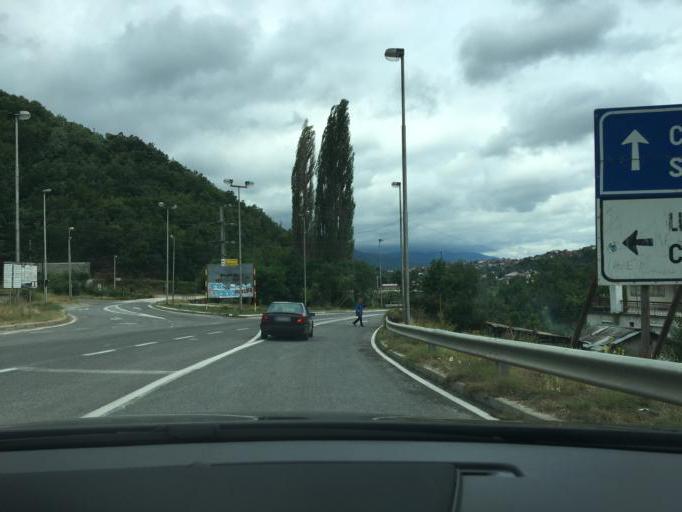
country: MK
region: Kriva Palanka
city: Kriva Palanka
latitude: 42.2130
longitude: 22.3464
